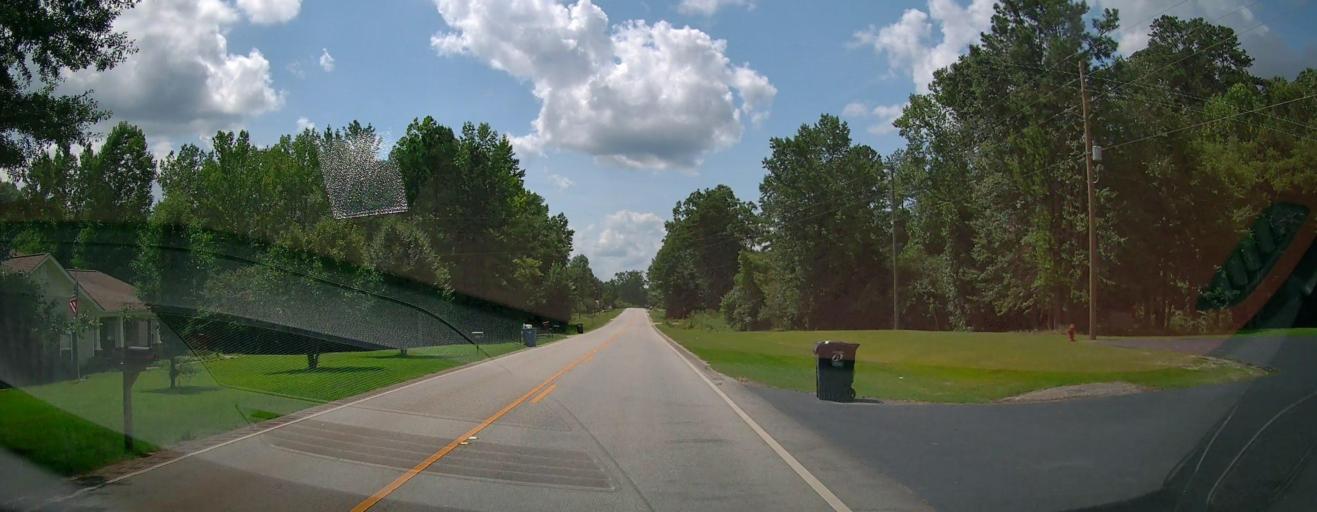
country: US
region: Alabama
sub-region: Cleburne County
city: Heflin
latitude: 33.5749
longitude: -85.4541
